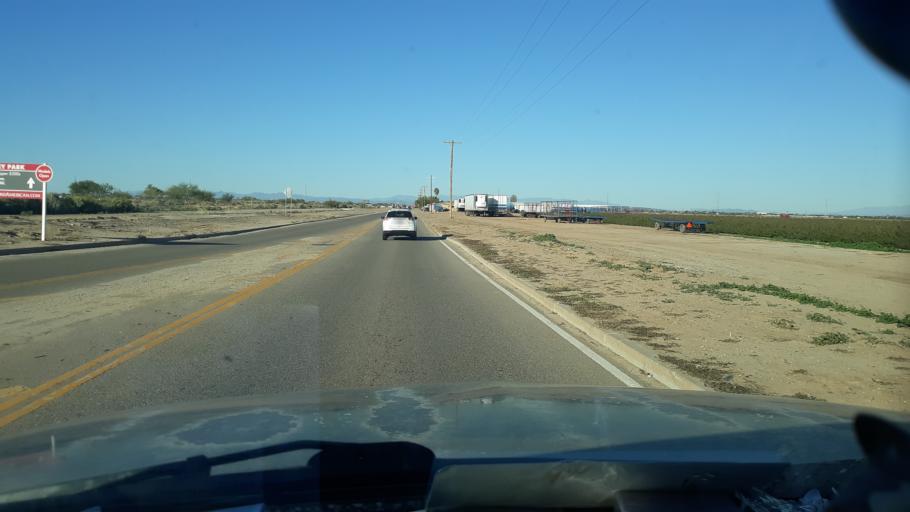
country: US
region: Arizona
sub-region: Maricopa County
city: Citrus Park
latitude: 33.5604
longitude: -112.3935
